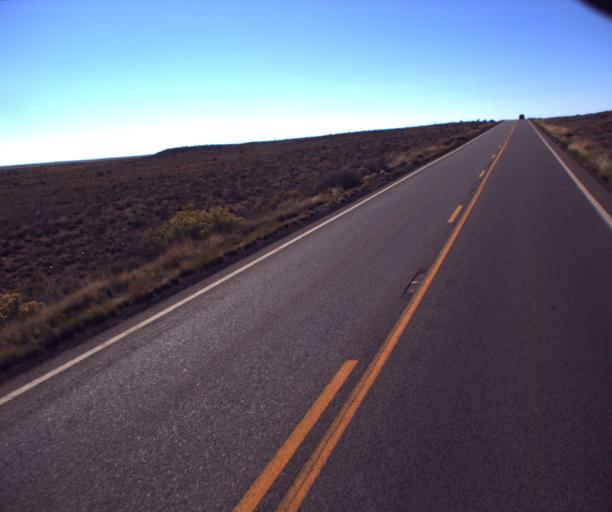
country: US
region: Arizona
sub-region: Navajo County
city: Dilkon
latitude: 35.2564
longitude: -110.4298
